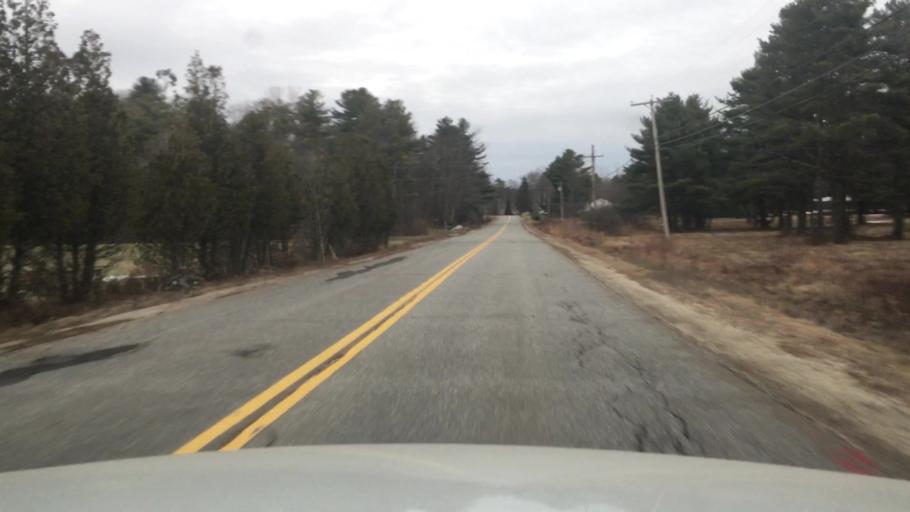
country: US
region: Maine
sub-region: Cumberland County
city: Brunswick
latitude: 43.8914
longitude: -70.0050
